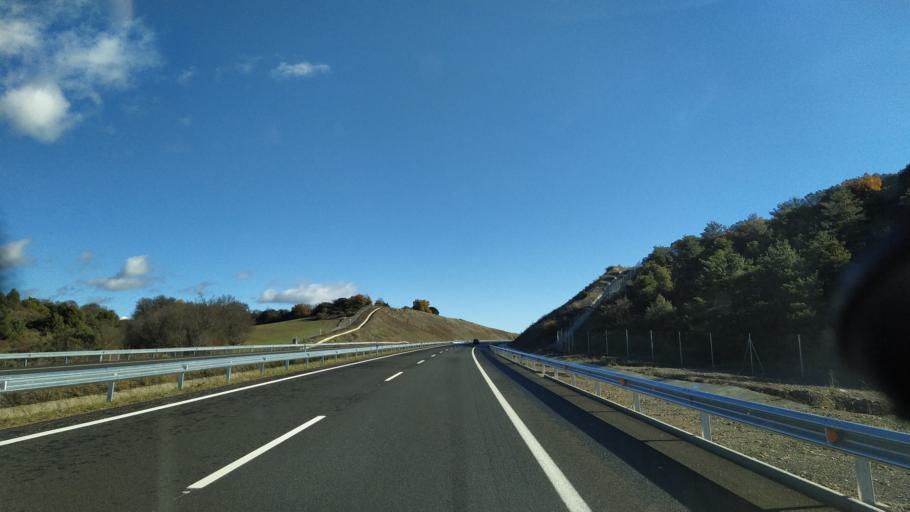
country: ES
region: Aragon
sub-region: Provincia de Huesca
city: Santa Cruz de la Seros
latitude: 42.5633
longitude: -0.6845
